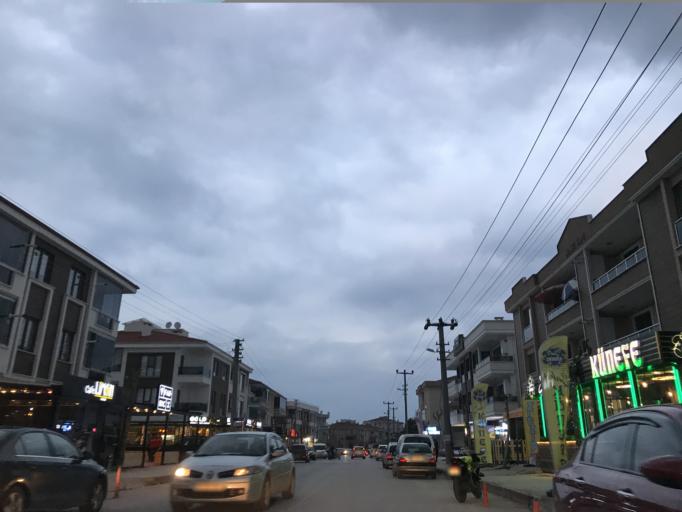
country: TR
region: Yalova
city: Yalova
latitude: 40.6453
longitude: 29.2599
